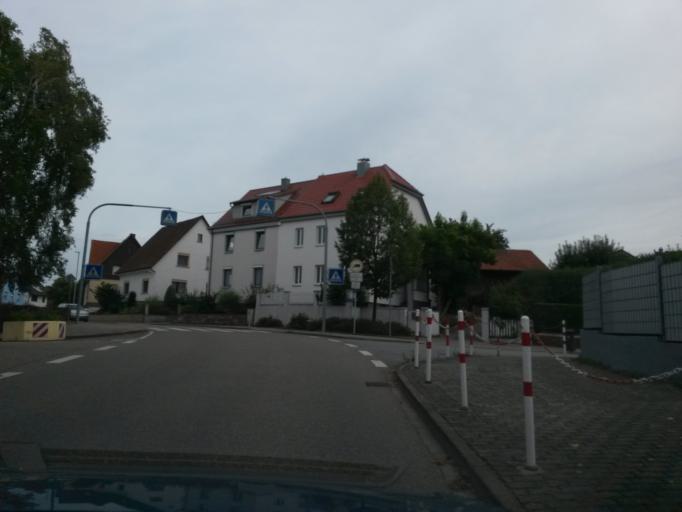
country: DE
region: Baden-Wuerttemberg
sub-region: Karlsruhe Region
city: Konigsbach-Stein
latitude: 48.9483
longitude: 8.5760
